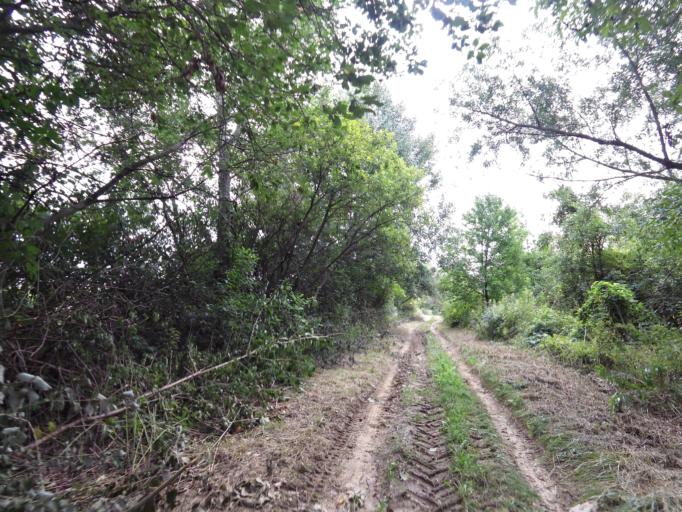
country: HU
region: Veszprem
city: Tapolca
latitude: 46.8312
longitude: 17.3709
